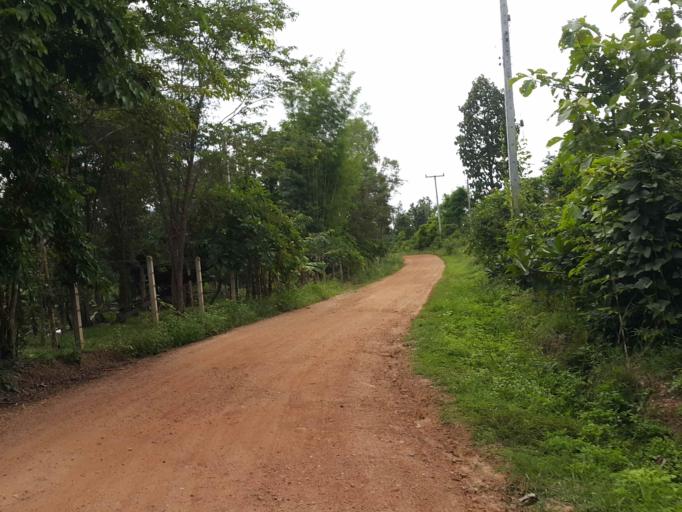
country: TH
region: Chiang Mai
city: San Sai
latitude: 18.9460
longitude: 98.9133
